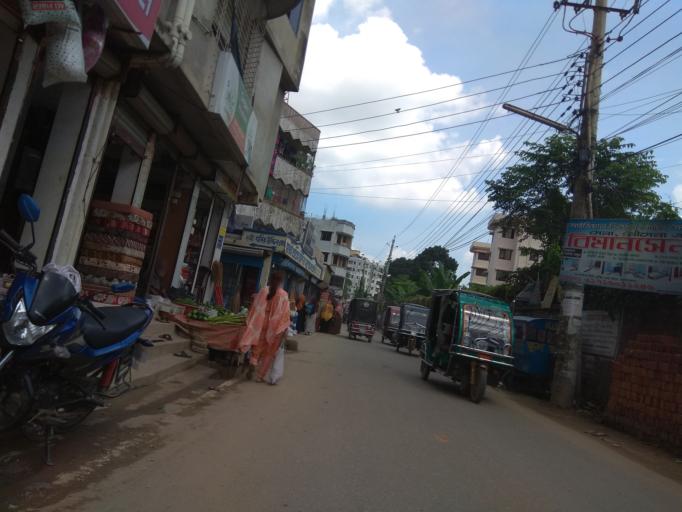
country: BD
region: Dhaka
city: Tungi
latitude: 23.8306
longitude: 90.3902
